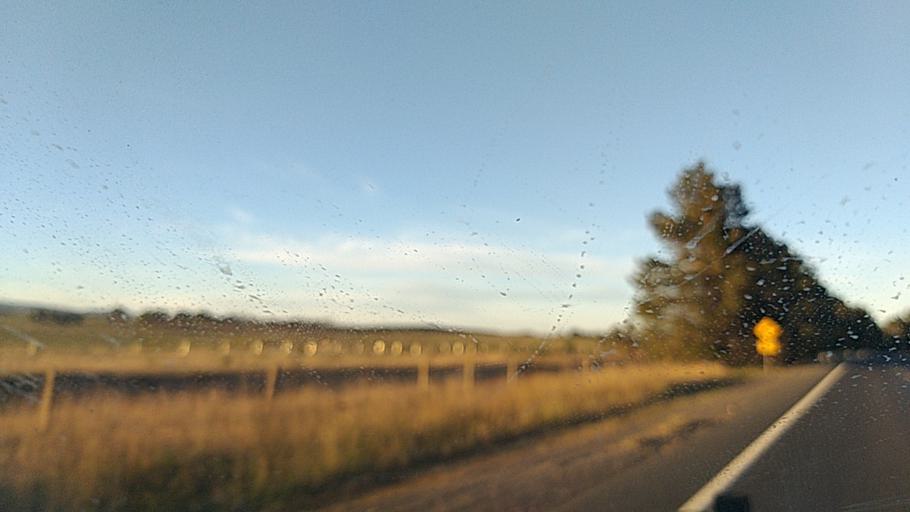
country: AU
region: New South Wales
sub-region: Goulburn Mulwaree
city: Goulburn
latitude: -34.8732
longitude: 149.5439
